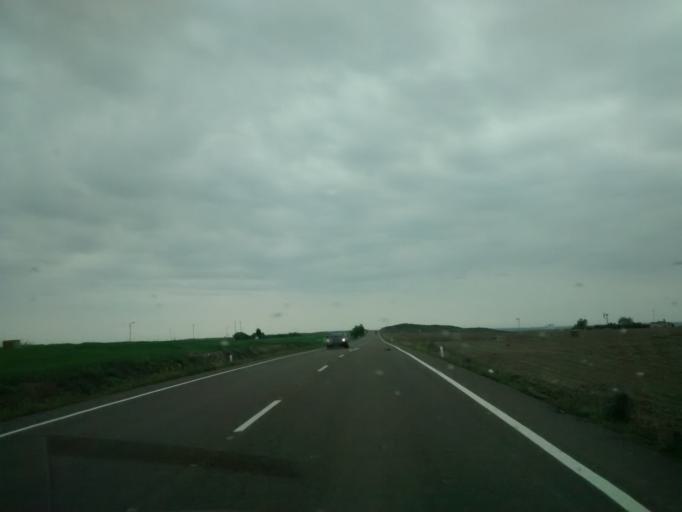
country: ES
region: Aragon
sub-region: Provincia de Zaragoza
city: Bujaraloz
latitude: 41.5167
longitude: -0.1731
